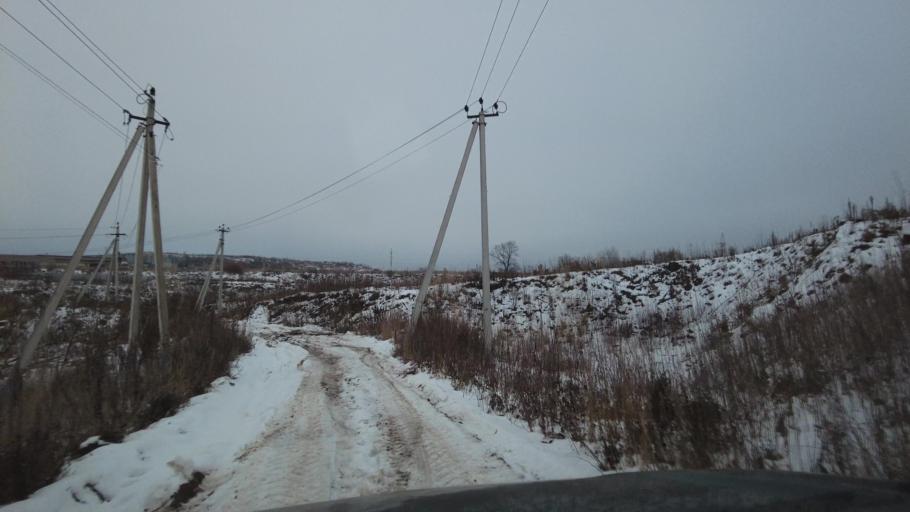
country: RU
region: Moskovskaya
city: Novopodrezkovo
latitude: 55.9893
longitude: 37.3929
